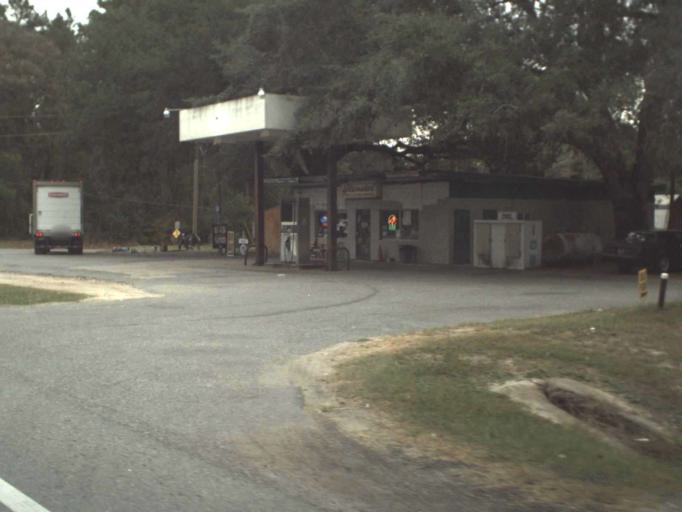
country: US
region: Florida
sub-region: Wakulla County
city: Crawfordville
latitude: 30.2814
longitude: -84.3543
